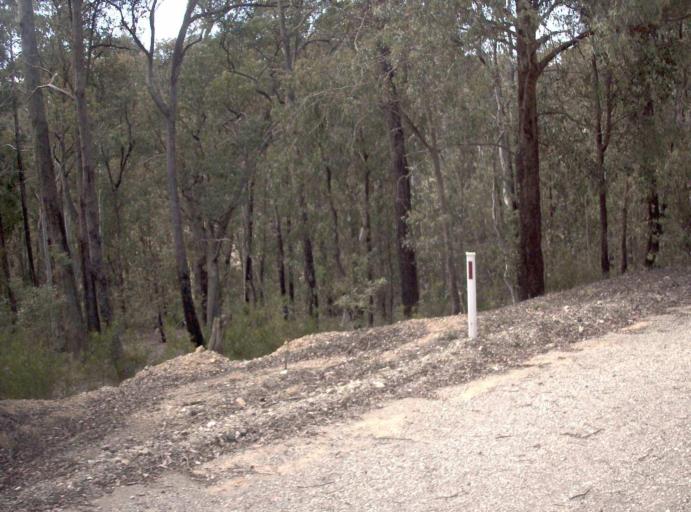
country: AU
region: New South Wales
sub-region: Bombala
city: Bombala
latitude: -37.1823
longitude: 148.7097
